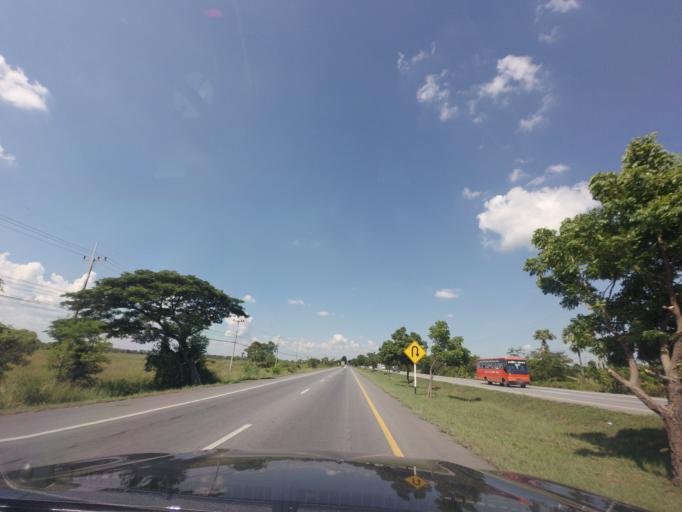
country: TH
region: Nakhon Ratchasima
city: Non Sung
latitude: 15.1338
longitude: 102.3092
